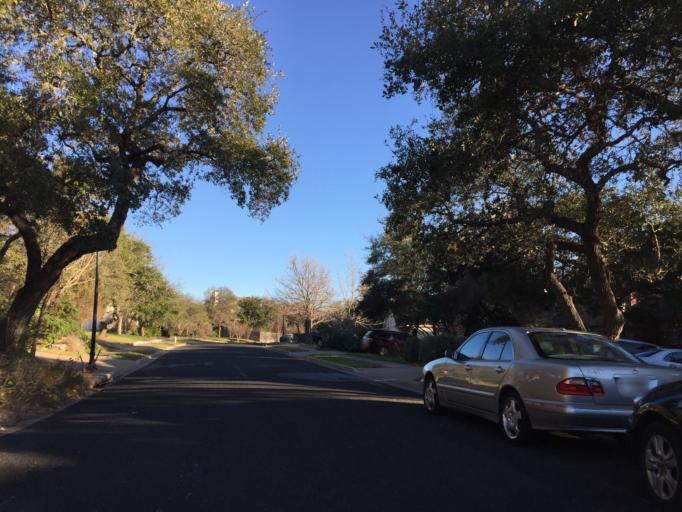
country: US
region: Texas
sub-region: Williamson County
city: Jollyville
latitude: 30.4333
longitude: -97.7883
